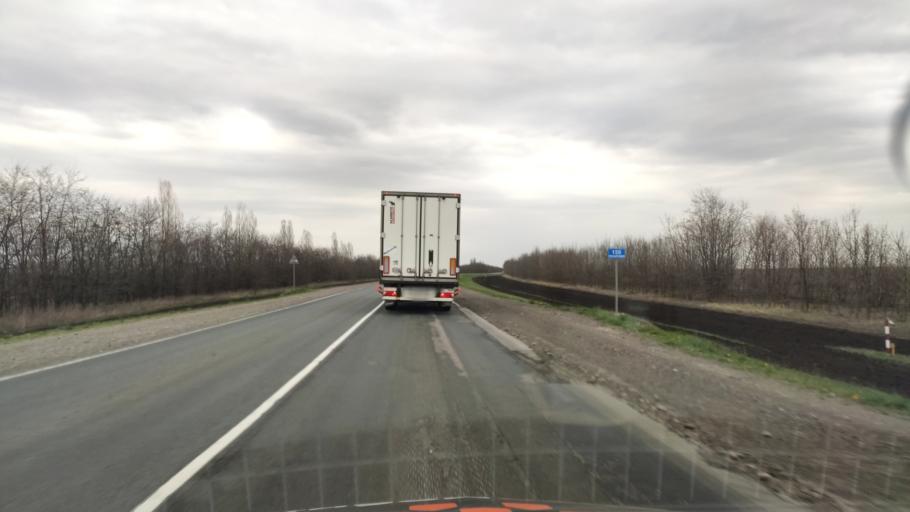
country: RU
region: Voronezj
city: Nizhnedevitsk
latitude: 51.5750
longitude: 38.3247
